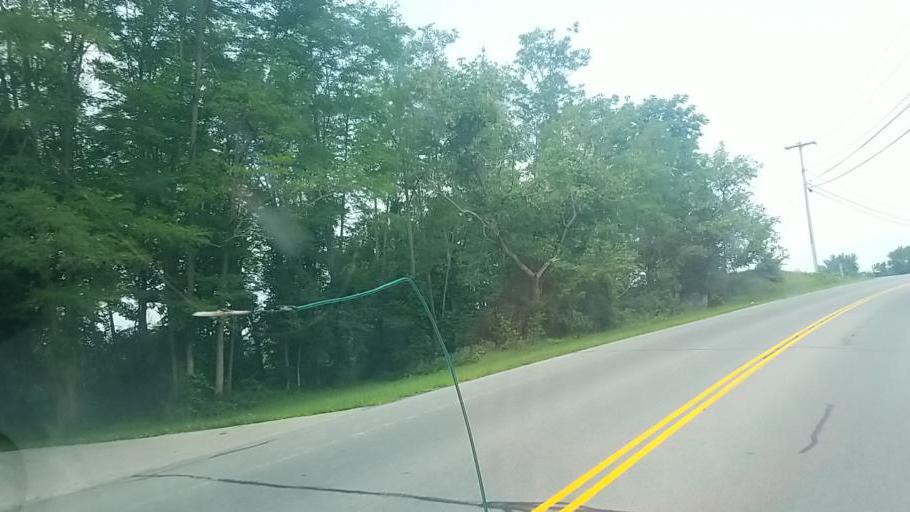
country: US
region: New York
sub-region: Montgomery County
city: Fort Plain
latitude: 42.9430
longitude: -74.6191
